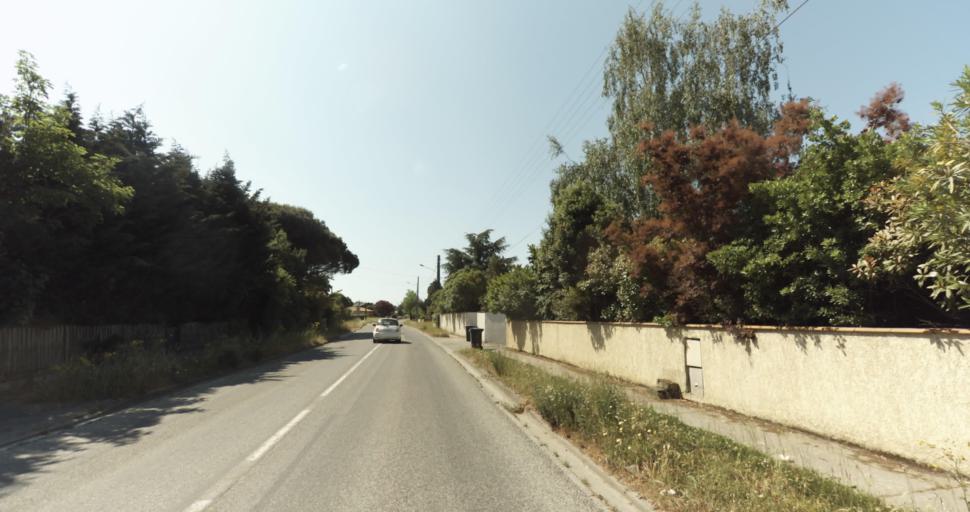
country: FR
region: Midi-Pyrenees
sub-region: Departement de la Haute-Garonne
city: Plaisance-du-Touch
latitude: 43.5805
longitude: 1.2902
